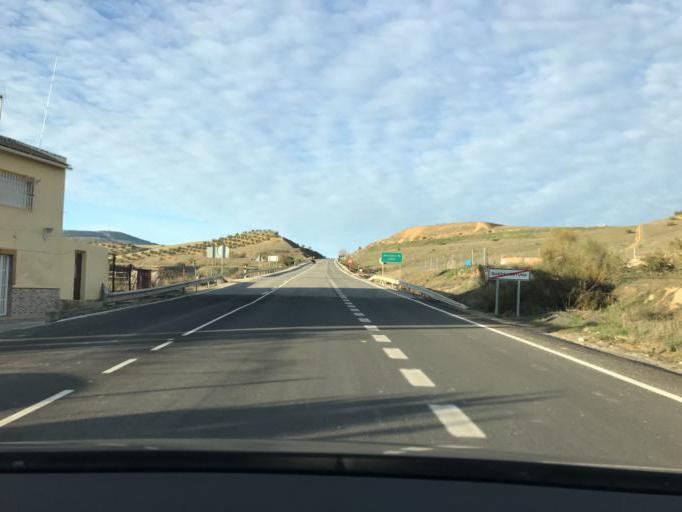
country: ES
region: Andalusia
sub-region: Provincia de Jaen
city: Guadahortuna
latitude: 37.5638
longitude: -3.4010
